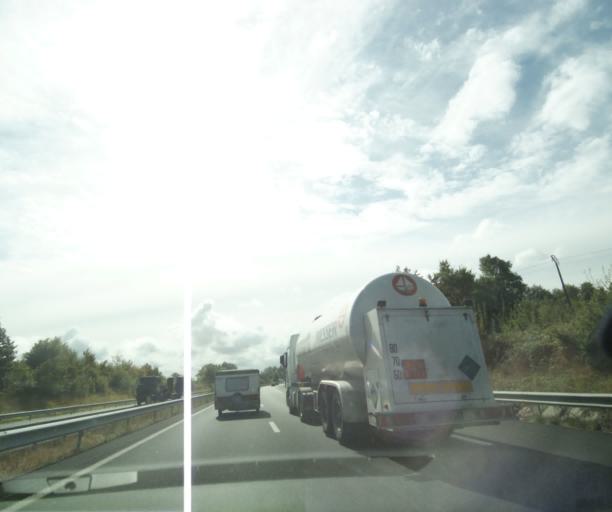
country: FR
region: Poitou-Charentes
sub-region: Departement de la Charente-Maritime
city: Pons
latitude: 45.6031
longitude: -0.5915
